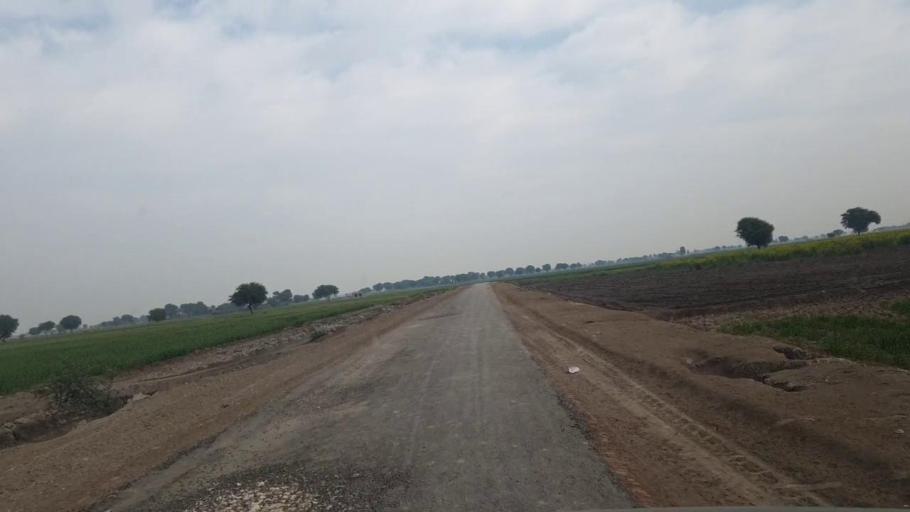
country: PK
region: Sindh
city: Shahdadpur
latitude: 25.9532
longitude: 68.6708
